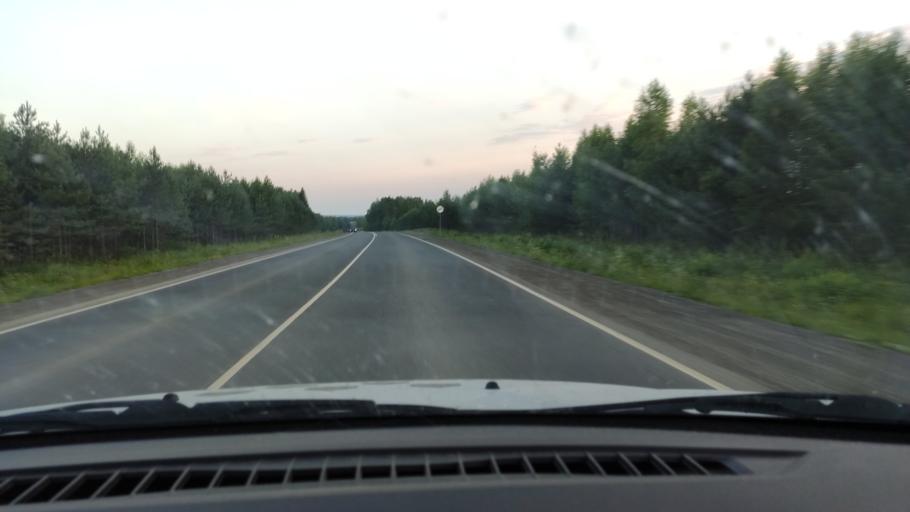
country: RU
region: Perm
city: Siva
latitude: 58.4325
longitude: 54.4405
